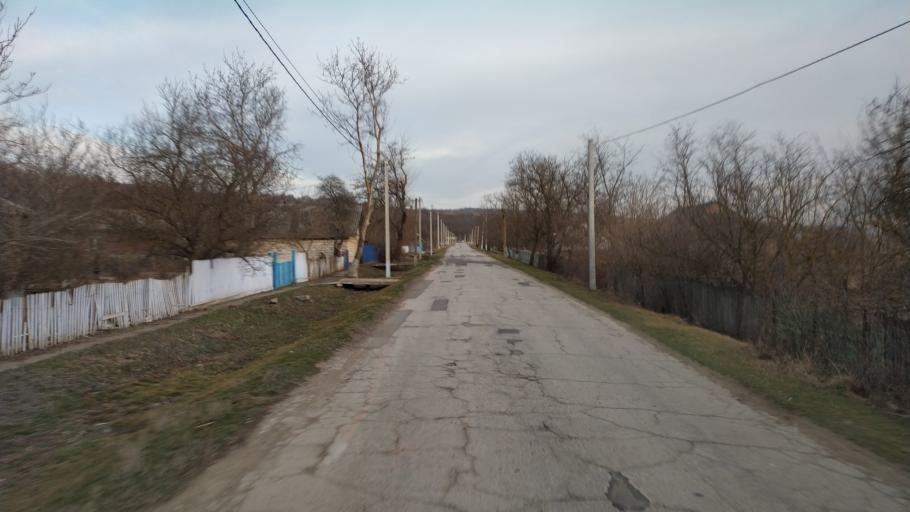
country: MD
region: Hincesti
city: Dancu
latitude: 46.7877
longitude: 28.1905
